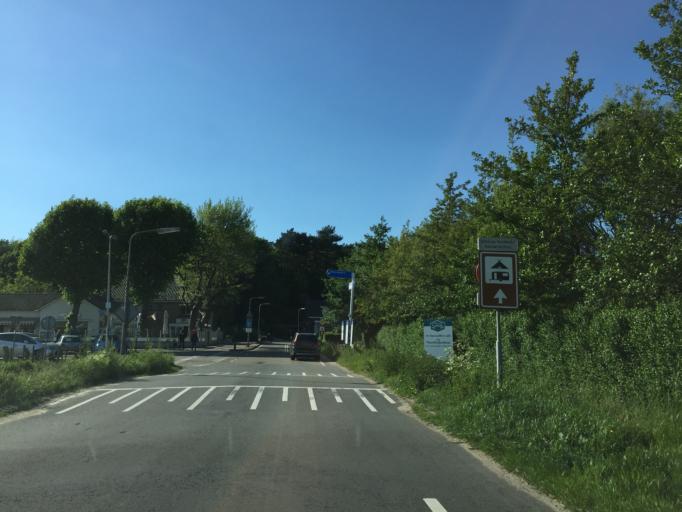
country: NL
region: South Holland
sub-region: Gemeente Noordwijkerhout
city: Noordwijkerhout
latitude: 52.2693
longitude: 4.4680
